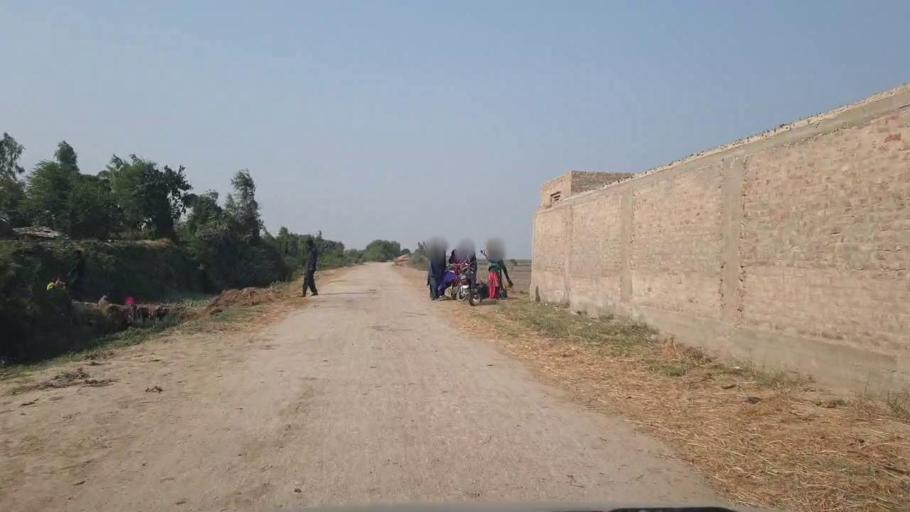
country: PK
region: Sindh
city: Tando Muhammad Khan
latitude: 25.0576
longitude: 68.3639
